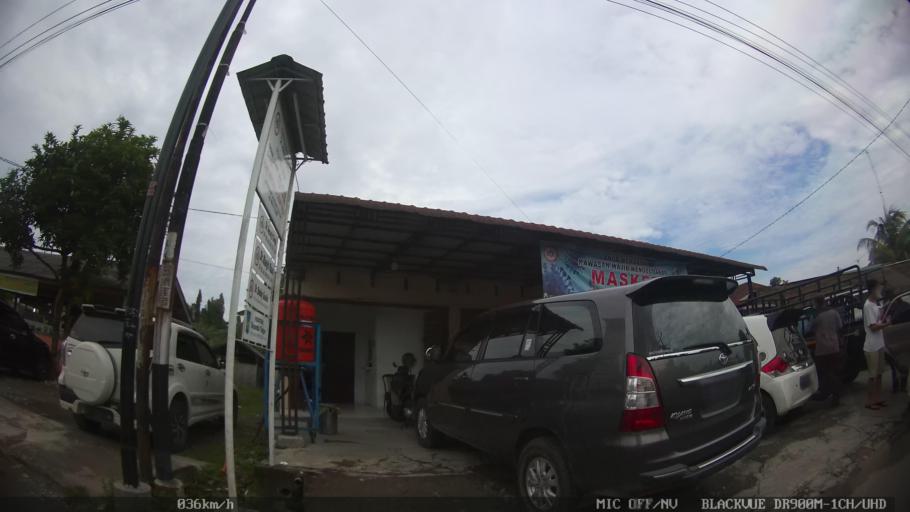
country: ID
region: North Sumatra
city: Sunggal
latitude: 3.6529
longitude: 98.5953
